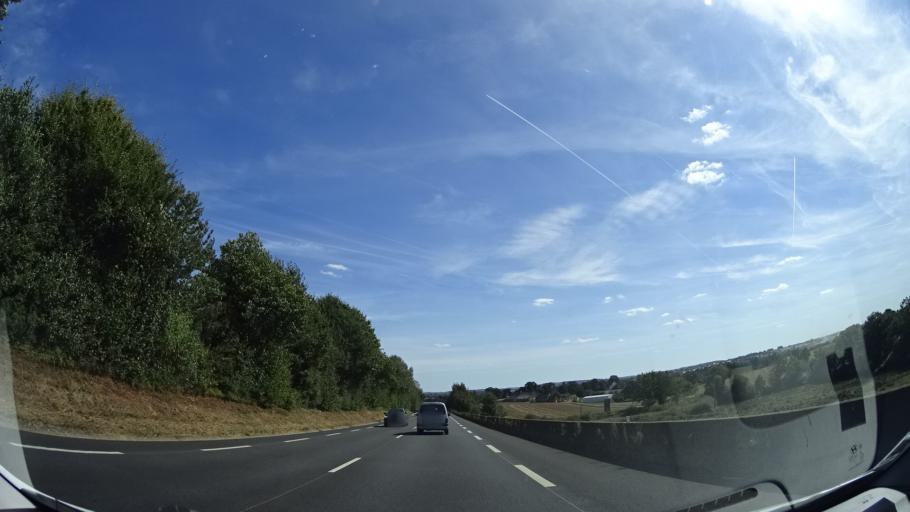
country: FR
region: Brittany
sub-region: Departement d'Ille-et-Vilaine
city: Lecousse
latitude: 48.3444
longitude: -1.2237
